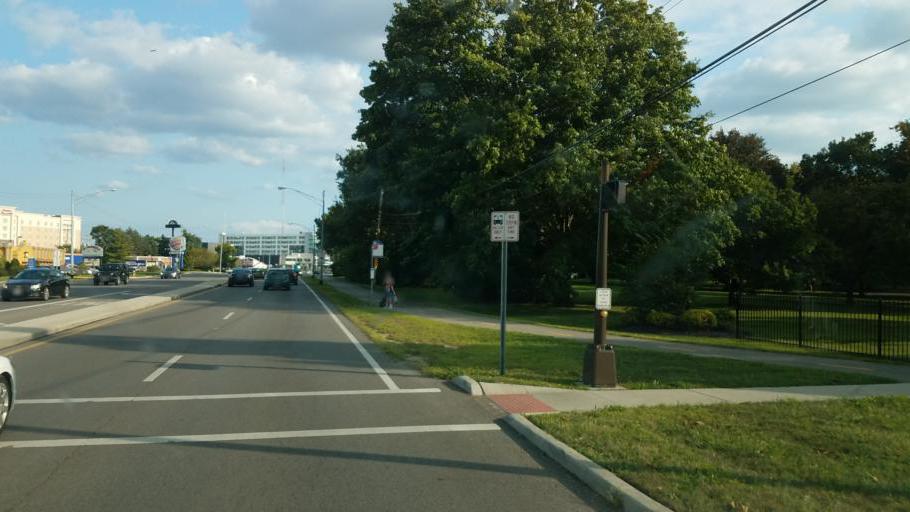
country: US
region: Ohio
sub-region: Franklin County
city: Upper Arlington
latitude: 40.0274
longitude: -83.0280
